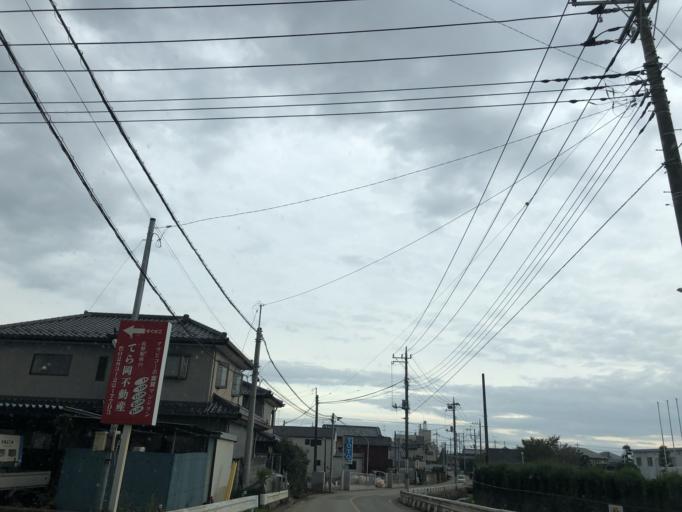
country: JP
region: Tochigi
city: Sano
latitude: 36.3160
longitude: 139.5710
